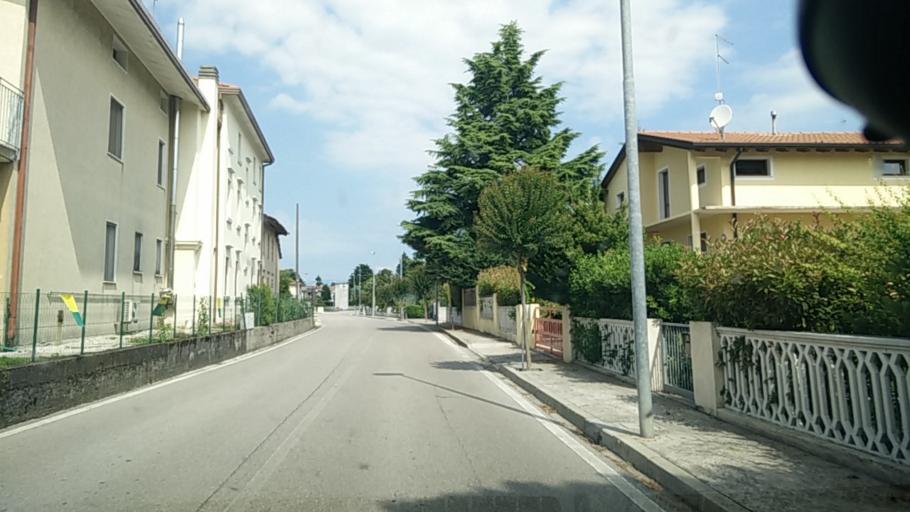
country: IT
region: Friuli Venezia Giulia
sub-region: Provincia di Pordenone
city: Puia-Villanova
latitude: 45.8442
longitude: 12.5652
